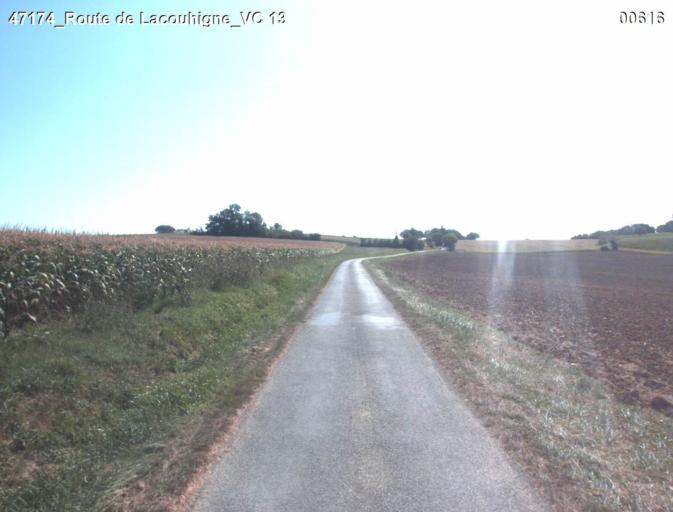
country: FR
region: Midi-Pyrenees
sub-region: Departement du Gers
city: Condom
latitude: 44.0201
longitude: 0.3853
